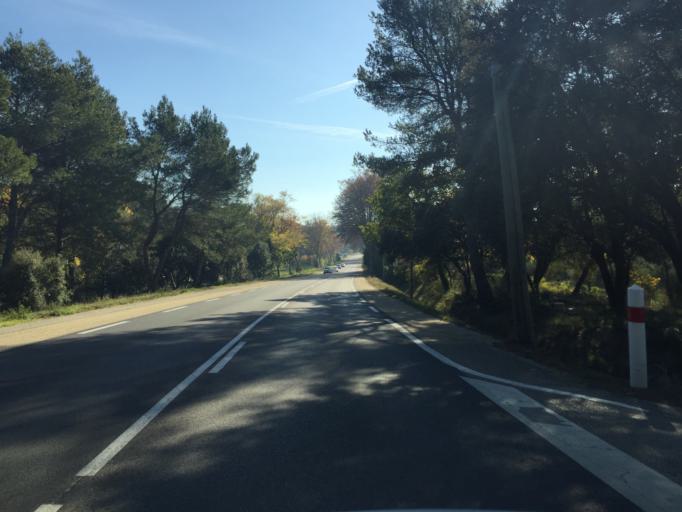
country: FR
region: Provence-Alpes-Cote d'Azur
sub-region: Departement des Bouches-du-Rhone
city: Orgon
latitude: 43.8084
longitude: 5.0254
